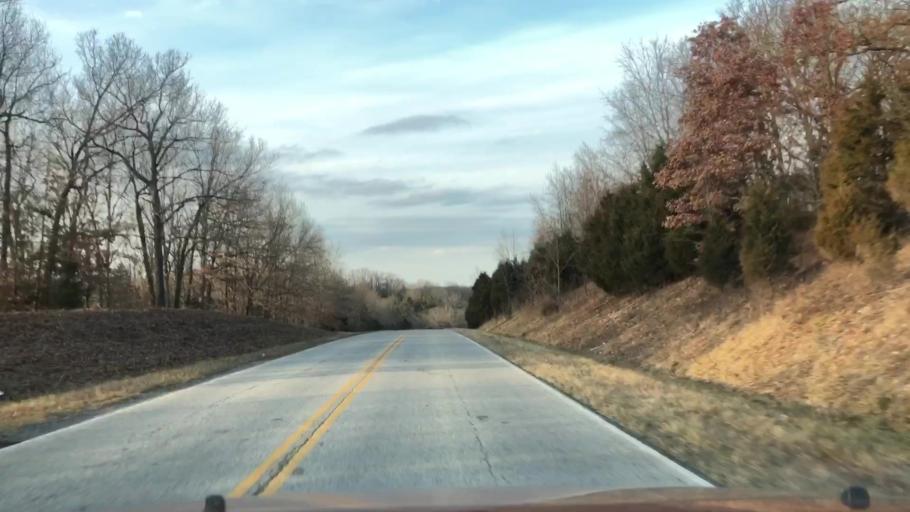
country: US
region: Missouri
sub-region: Webster County
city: Marshfield
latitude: 37.2369
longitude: -92.8793
